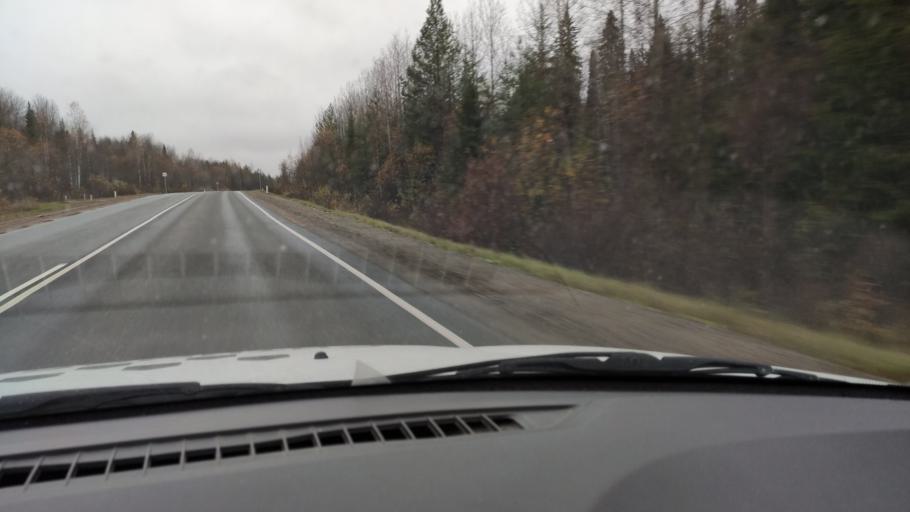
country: RU
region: Kirov
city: Omutninsk
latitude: 58.7008
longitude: 52.1144
